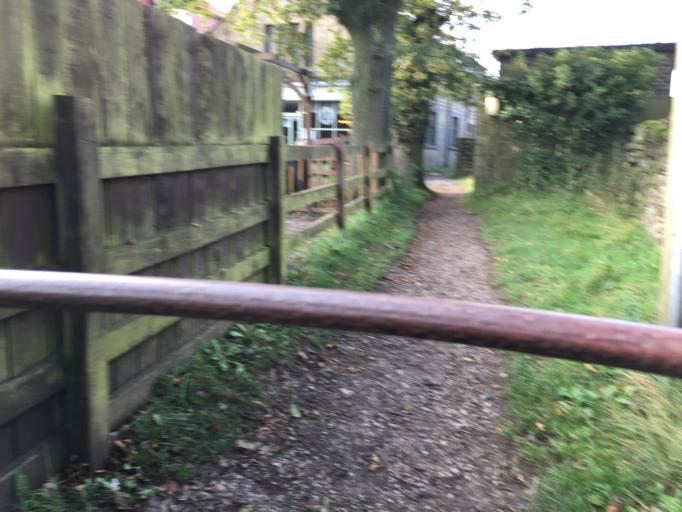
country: GB
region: England
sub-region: North Yorkshire
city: Sleights
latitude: 54.3955
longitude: -0.7269
